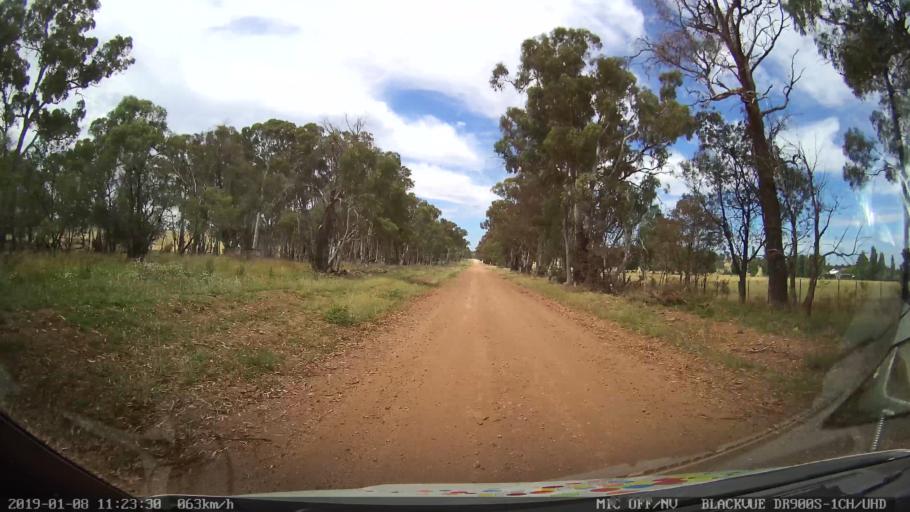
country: AU
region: New South Wales
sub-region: Guyra
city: Guyra
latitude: -30.2558
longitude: 151.5589
